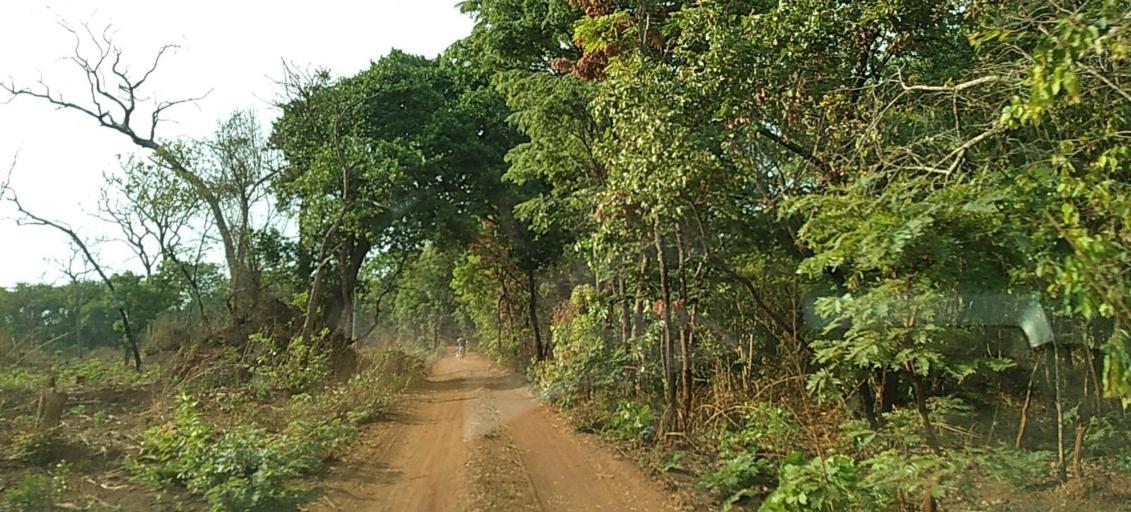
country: ZM
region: Copperbelt
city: Kalulushi
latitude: -12.9697
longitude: 27.7142
